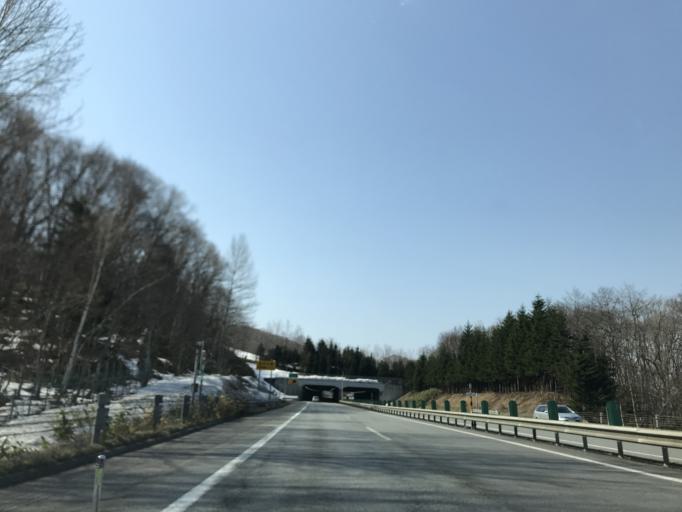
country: JP
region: Hokkaido
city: Bibai
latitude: 43.2913
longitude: 141.8652
